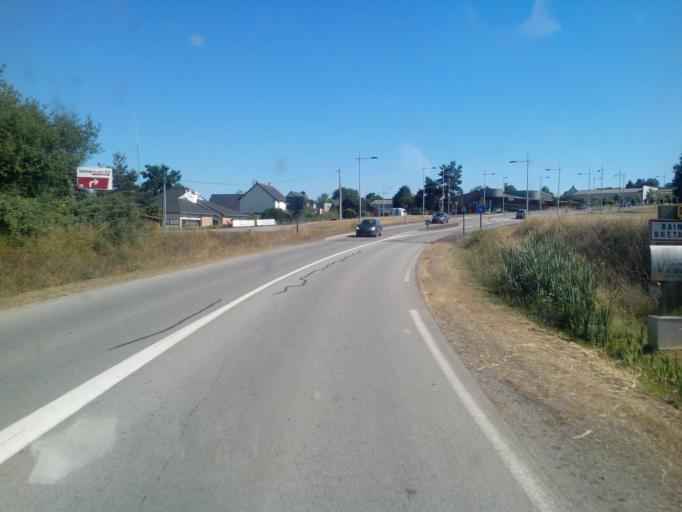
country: FR
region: Brittany
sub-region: Departement d'Ille-et-Vilaine
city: Bain-de-Bretagne
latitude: 47.8521
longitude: -1.6814
